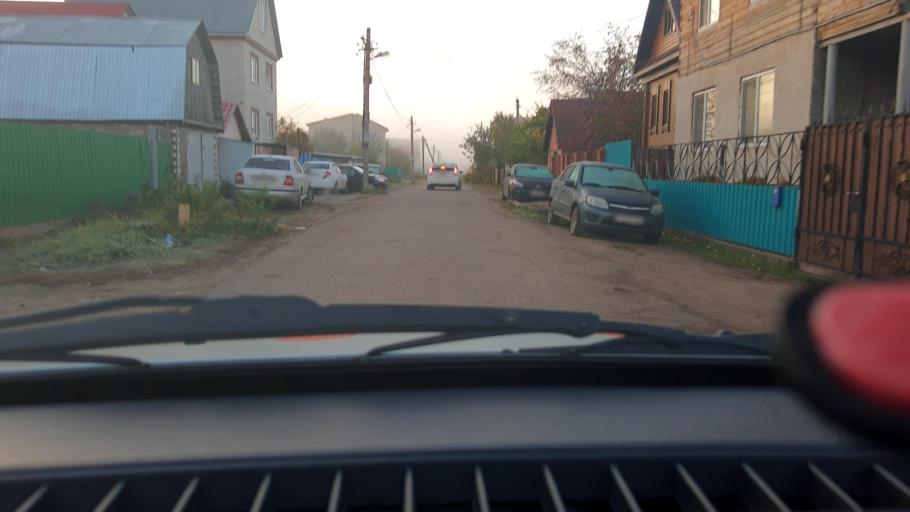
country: RU
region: Bashkortostan
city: Ufa
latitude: 54.7319
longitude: 55.9030
